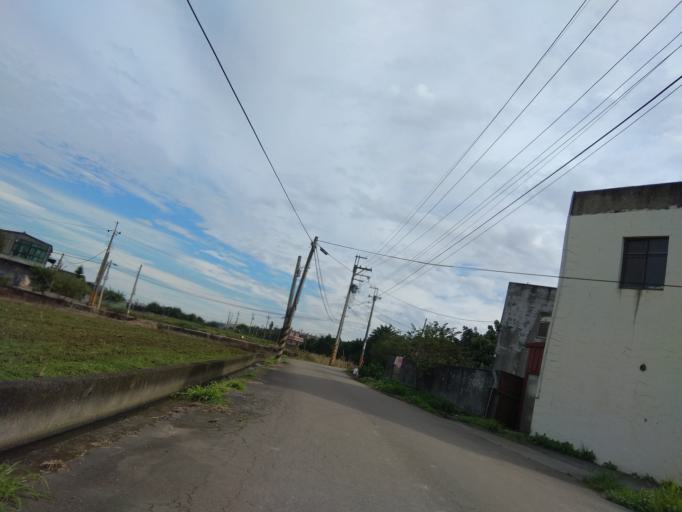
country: TW
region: Taiwan
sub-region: Hsinchu
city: Zhubei
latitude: 24.9481
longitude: 121.1078
